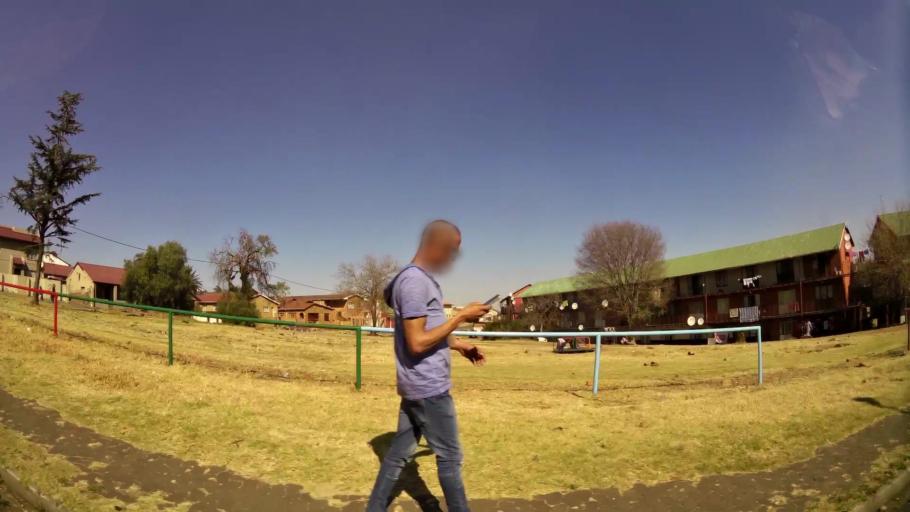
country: ZA
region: Gauteng
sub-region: City of Johannesburg Metropolitan Municipality
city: Johannesburg
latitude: -26.1878
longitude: 27.9657
